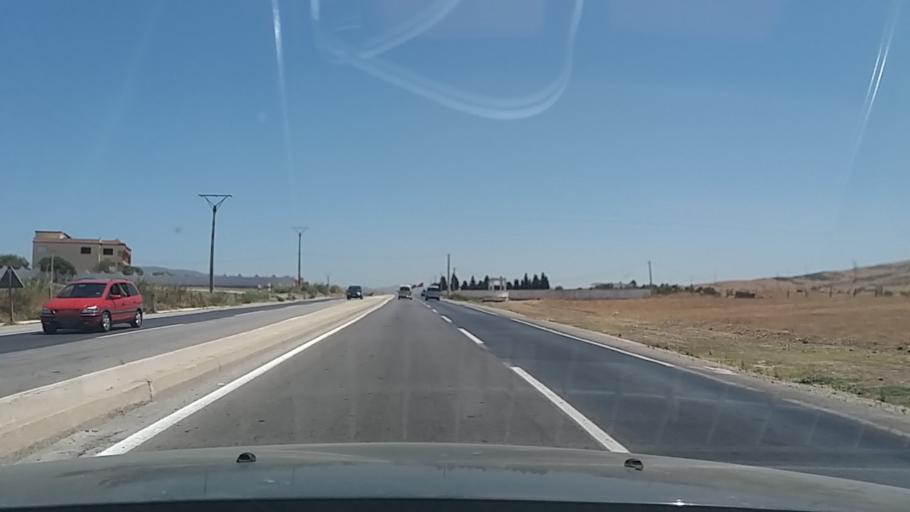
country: MA
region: Tanger-Tetouan
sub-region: Tanger-Assilah
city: Tangier
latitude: 35.6833
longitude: -5.7179
